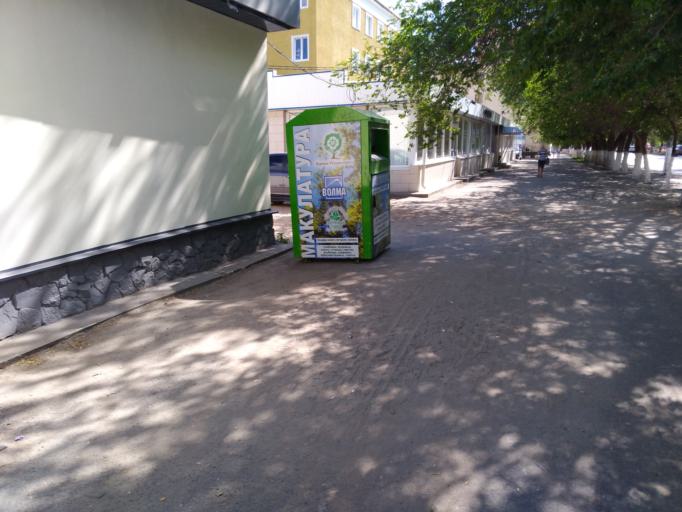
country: RU
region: Volgograd
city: Volgograd
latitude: 48.7108
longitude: 44.5132
